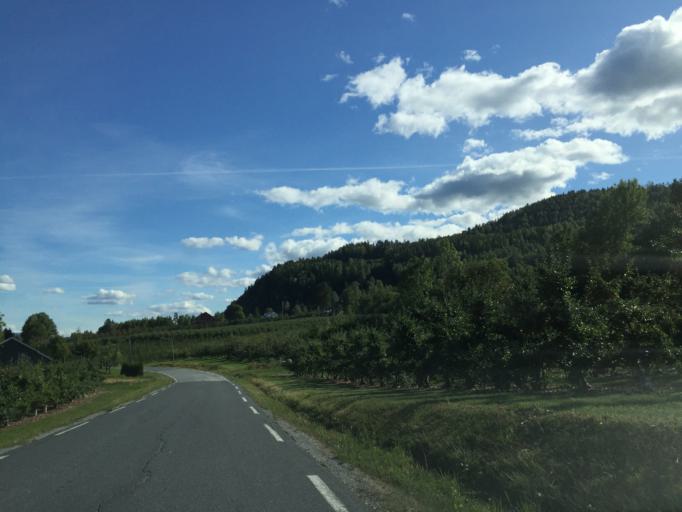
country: NO
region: Buskerud
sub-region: Ovre Eiker
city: Hokksund
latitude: 59.6880
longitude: 9.8493
